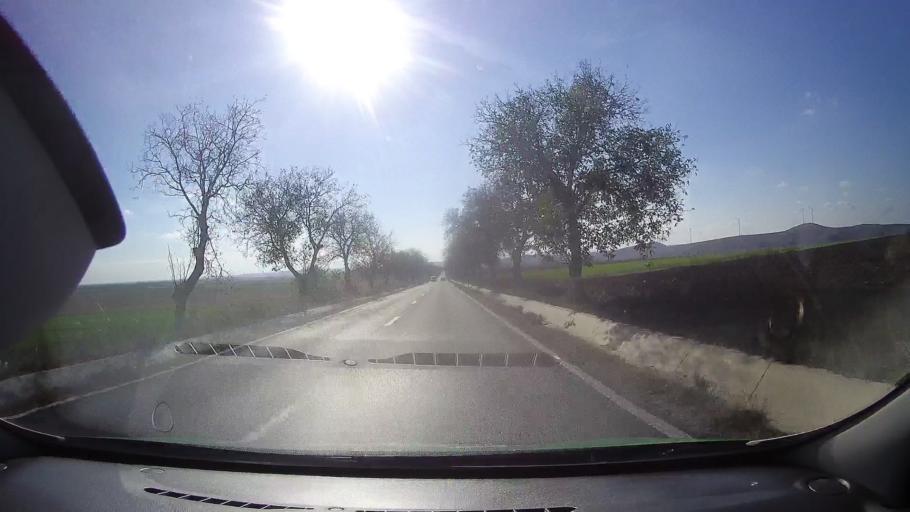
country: RO
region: Tulcea
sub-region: Comuna Ceamurlia de Jos
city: Ceamurlia de Jos
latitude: 44.8035
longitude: 28.6907
